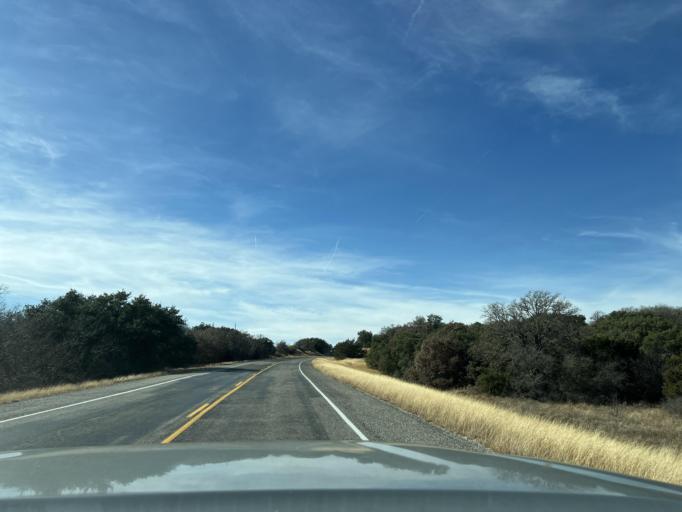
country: US
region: Texas
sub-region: Eastland County
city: Cisco
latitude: 32.4646
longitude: -99.0289
